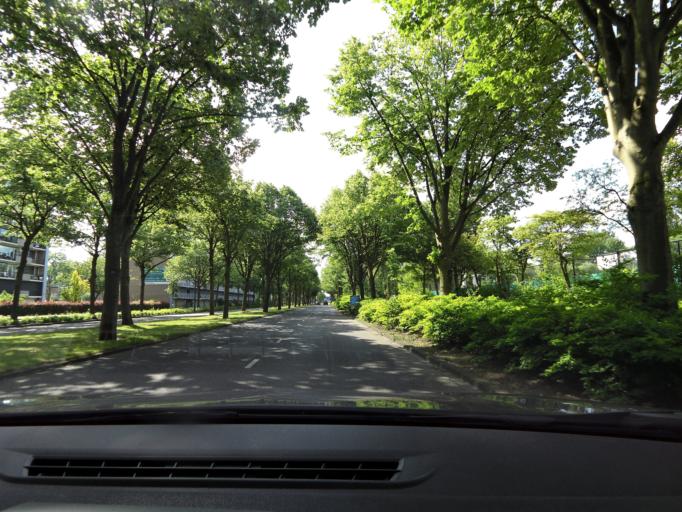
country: NL
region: South Holland
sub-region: Gemeente Vlaardingen
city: Vlaardingen
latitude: 51.9268
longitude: 4.3447
